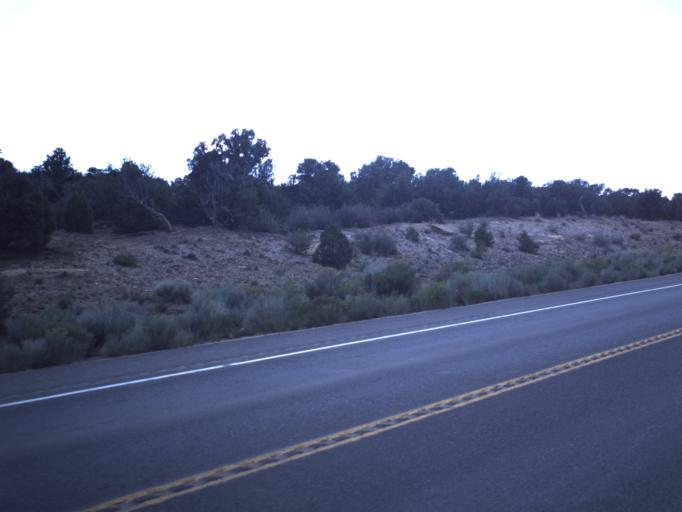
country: US
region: Utah
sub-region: Duchesne County
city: Duchesne
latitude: 40.1643
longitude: -110.4628
